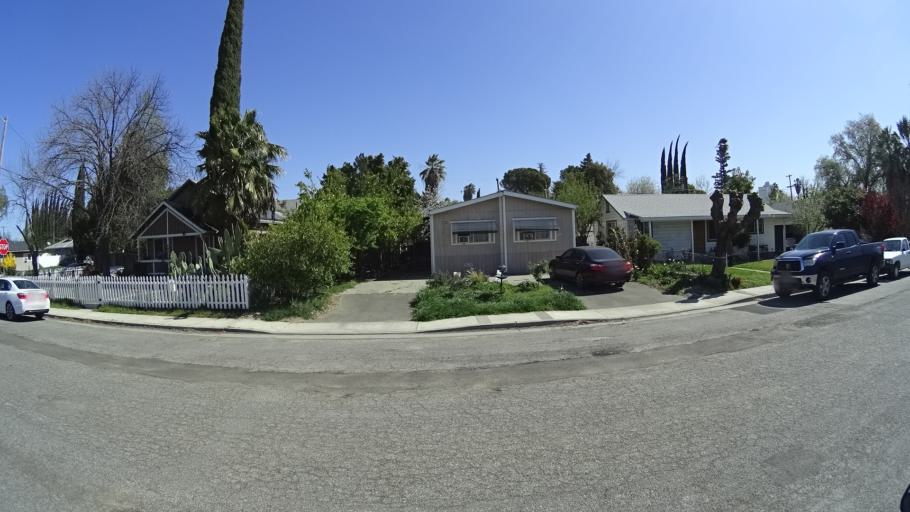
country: US
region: California
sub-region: Glenn County
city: Hamilton City
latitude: 39.7402
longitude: -122.0159
